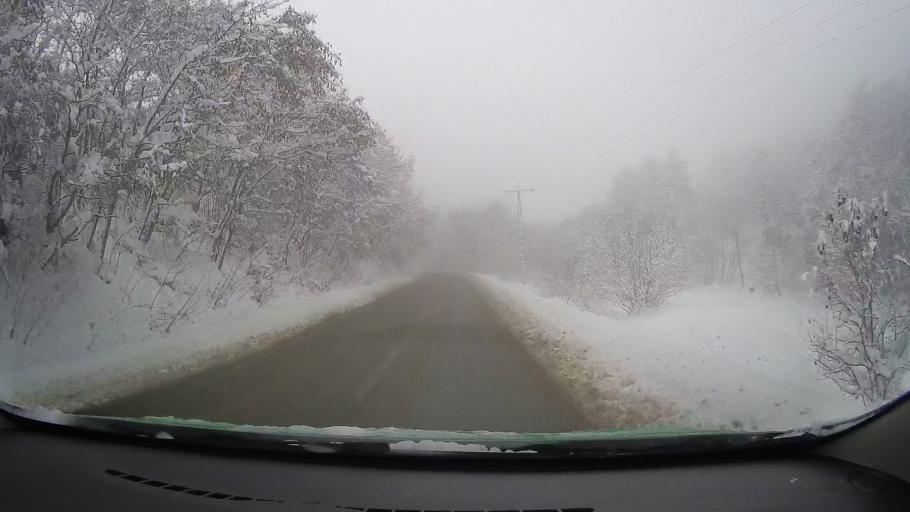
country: RO
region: Sibiu
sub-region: Comuna Poiana Sibiului
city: Poiana Sibiului
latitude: 45.8082
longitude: 23.7676
